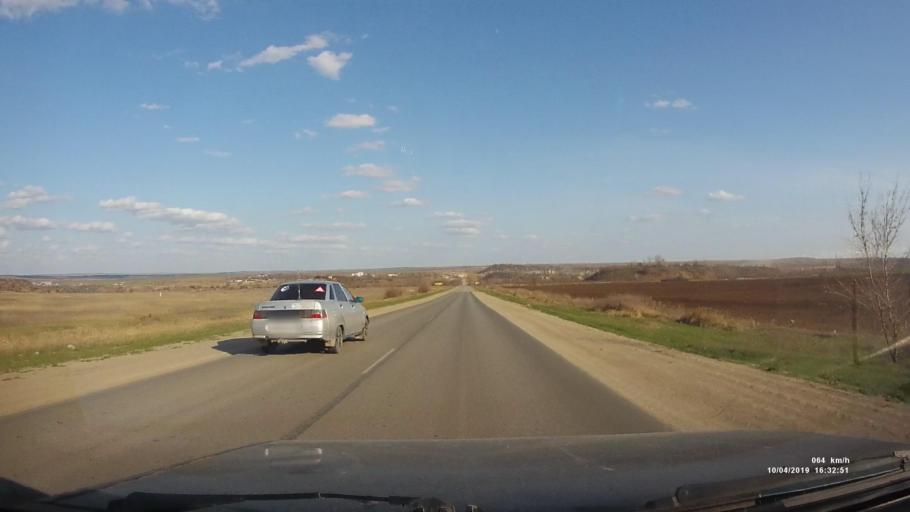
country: RU
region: Rostov
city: Staraya Stanitsa
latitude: 48.2445
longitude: 40.3907
